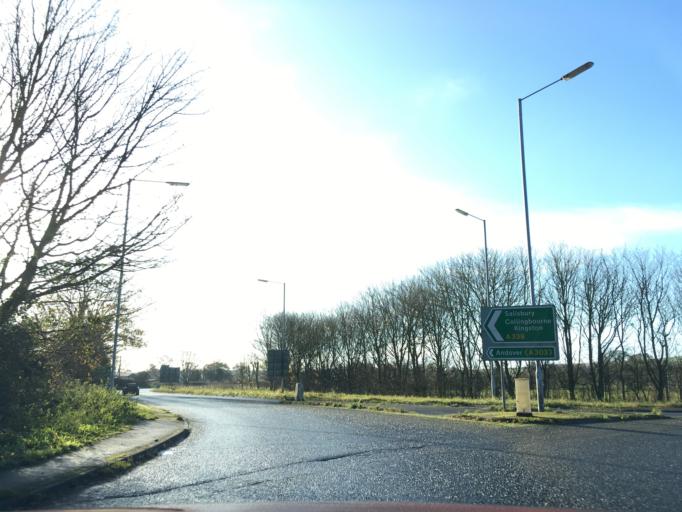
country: GB
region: England
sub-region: Wiltshire
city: Burbage
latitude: 51.3447
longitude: -1.6697
